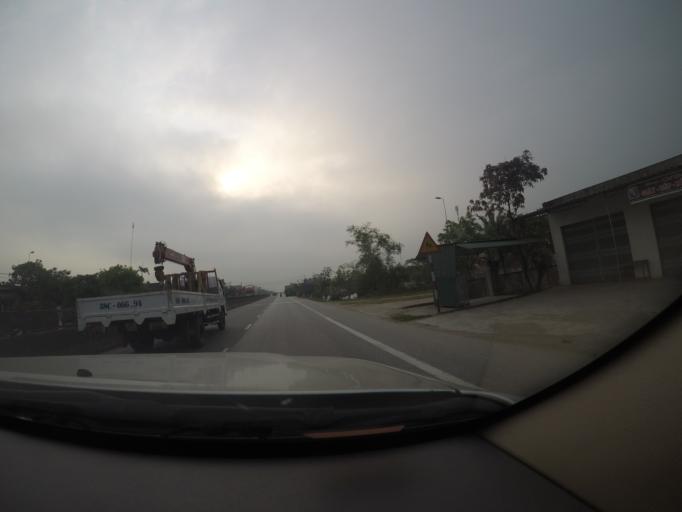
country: VN
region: Ha Tinh
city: Cam Xuyen
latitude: 18.2286
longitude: 106.0449
